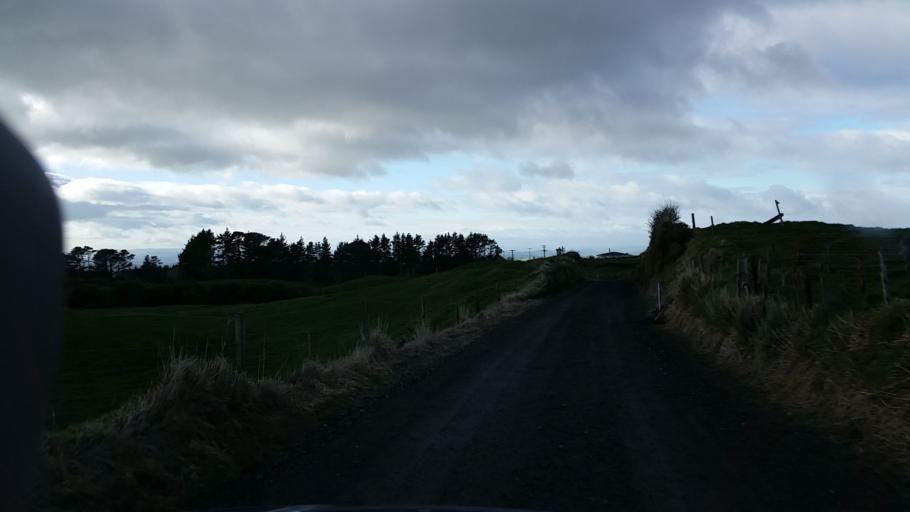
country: NZ
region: Taranaki
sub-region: South Taranaki District
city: Eltham
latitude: -39.3321
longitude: 174.1730
